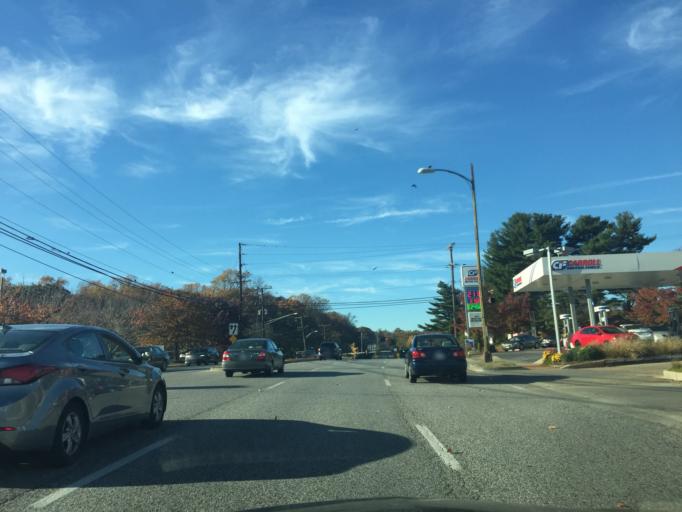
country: US
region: Maryland
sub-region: Baltimore County
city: Towson
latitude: 39.3859
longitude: -76.5781
